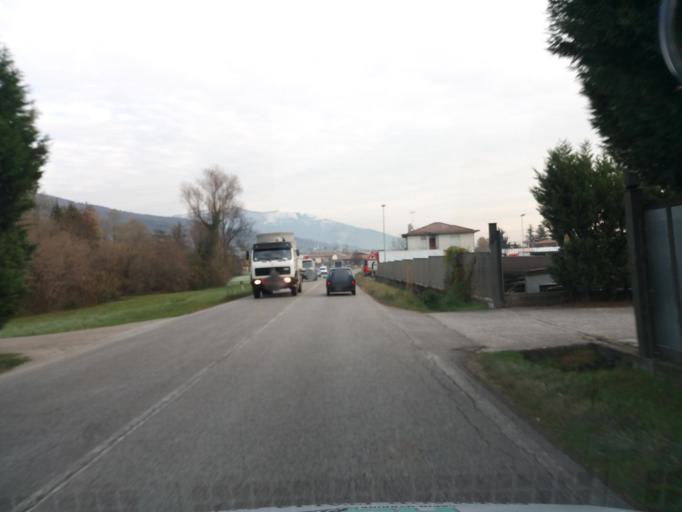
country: IT
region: Veneto
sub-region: Provincia di Treviso
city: Possagno
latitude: 45.8510
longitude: 11.8904
